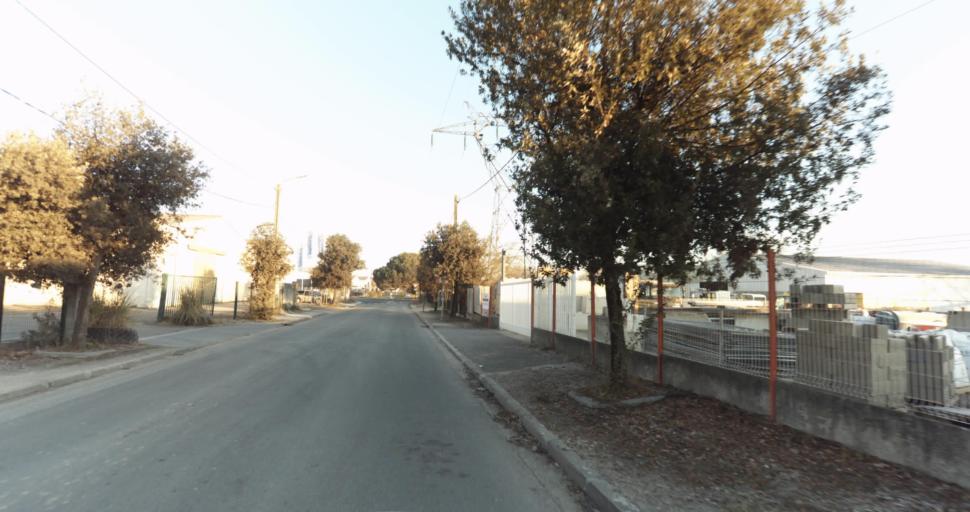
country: FR
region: Aquitaine
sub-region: Departement de la Gironde
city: Ambares-et-Lagrave
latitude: 44.9124
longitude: -0.4919
